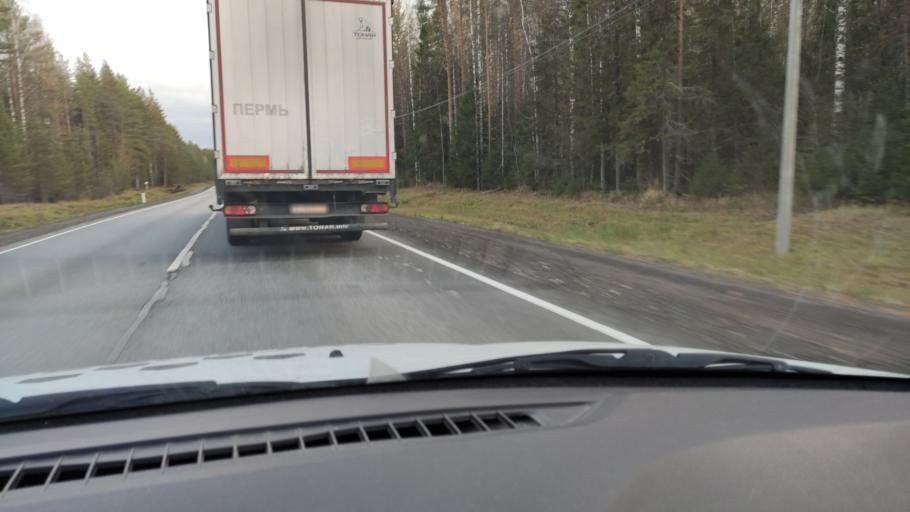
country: RU
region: Kirov
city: Dubrovka
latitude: 58.9089
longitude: 51.1782
